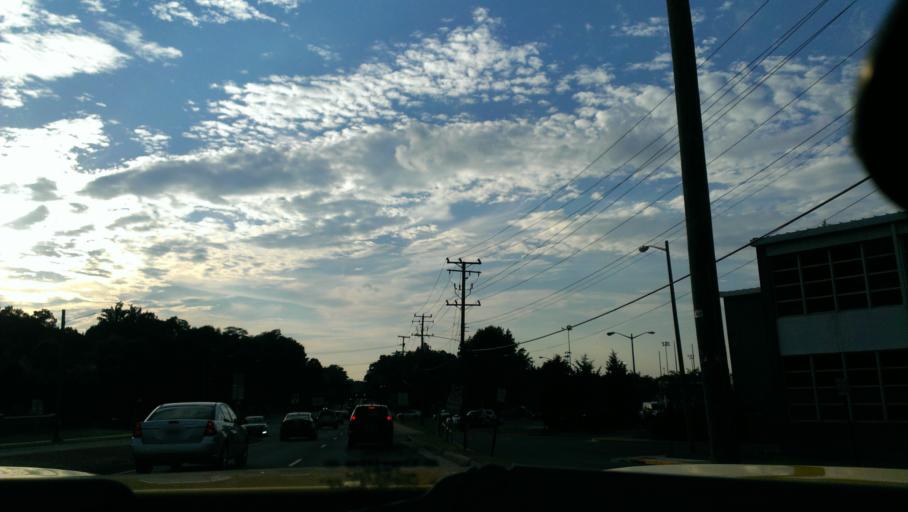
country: US
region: Virginia
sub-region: Fairfax County
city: Pimmit Hills
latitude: 38.8962
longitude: -77.1926
